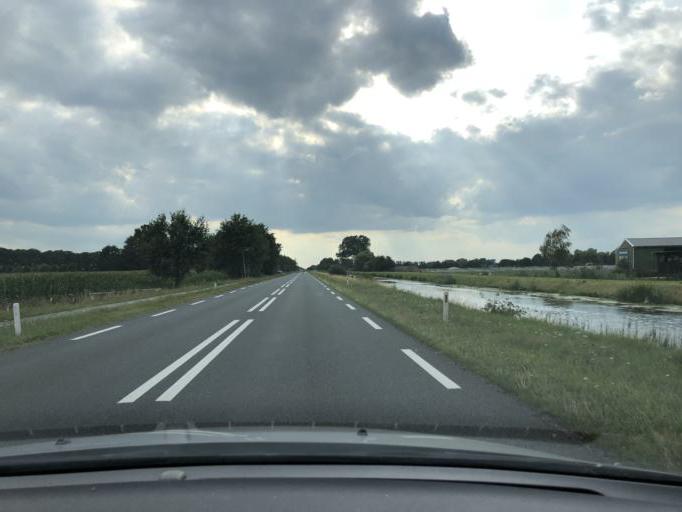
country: NL
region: Drenthe
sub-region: Gemeente Coevorden
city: Coevorden
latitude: 52.6566
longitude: 6.6897
